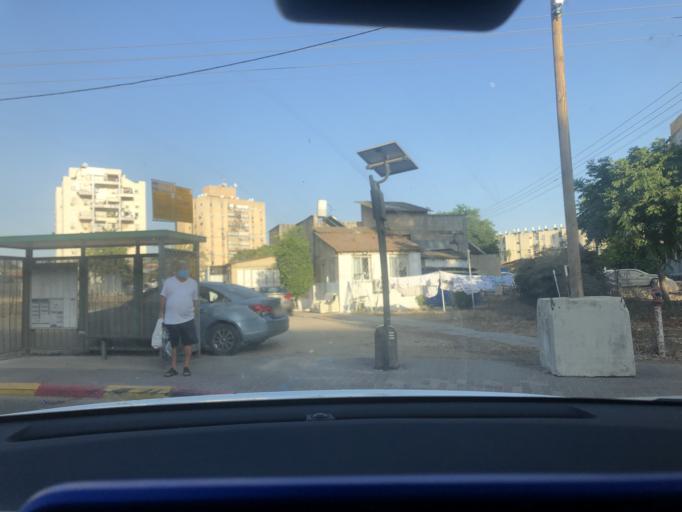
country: IL
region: Central District
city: Lod
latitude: 31.9463
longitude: 34.8793
